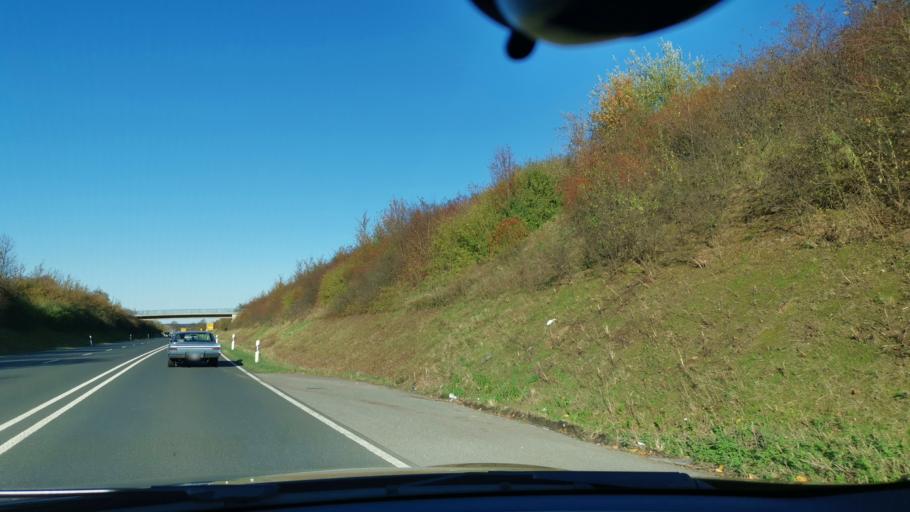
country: DE
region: North Rhine-Westphalia
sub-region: Regierungsbezirk Dusseldorf
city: Rommerskirchen
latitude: 51.0325
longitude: 6.6747
